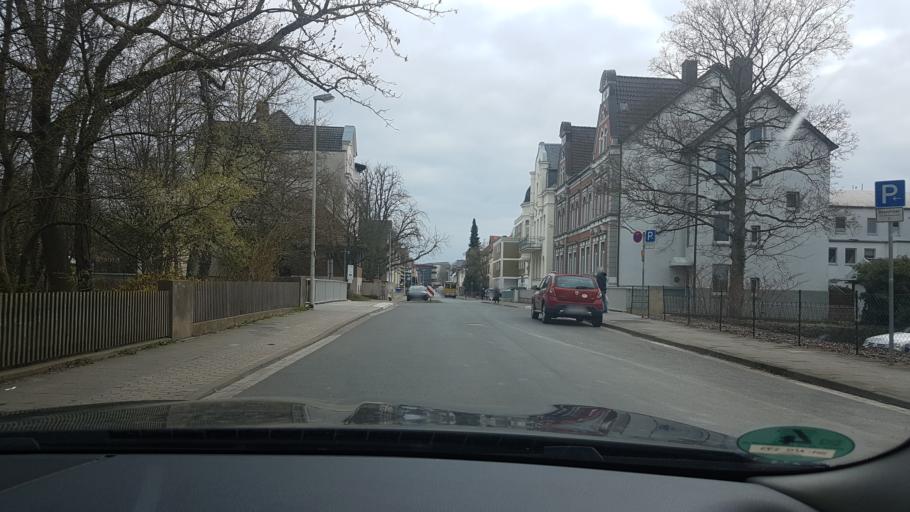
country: DE
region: Lower Saxony
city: Hameln
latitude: 52.1099
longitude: 9.3531
